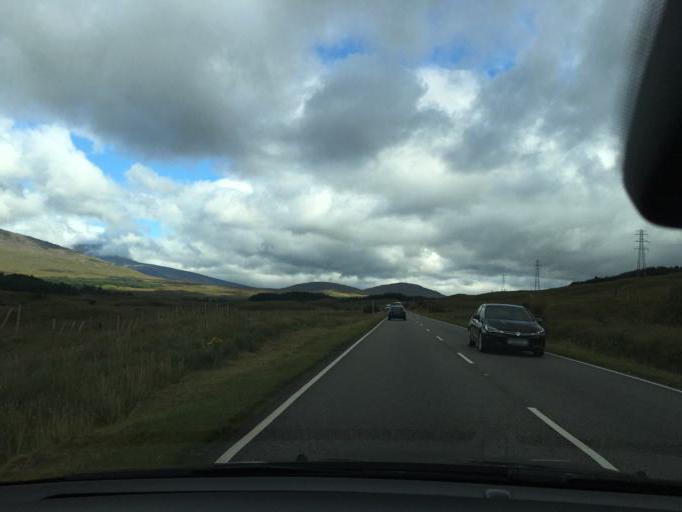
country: GB
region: Scotland
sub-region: Highland
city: Spean Bridge
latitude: 56.5259
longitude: -4.7670
